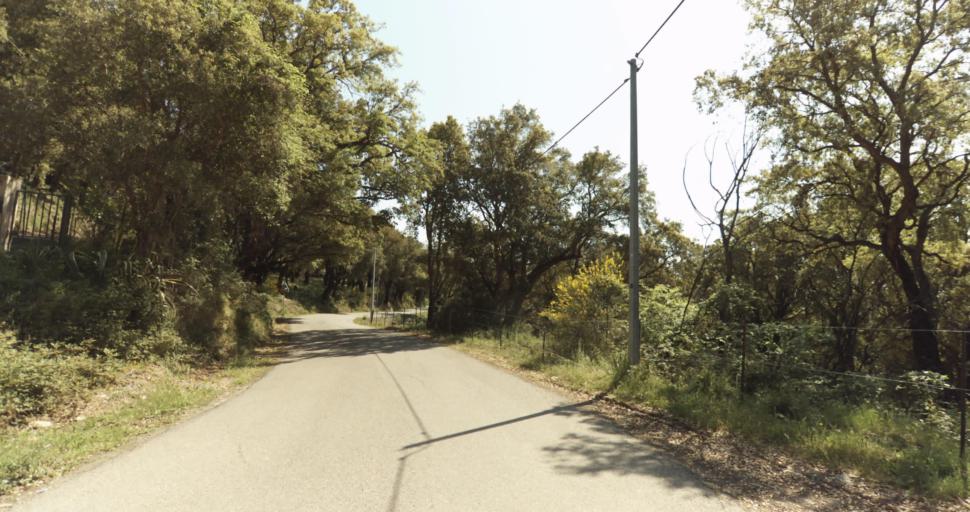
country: FR
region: Corsica
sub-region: Departement de la Haute-Corse
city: Biguglia
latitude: 42.6130
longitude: 9.4147
